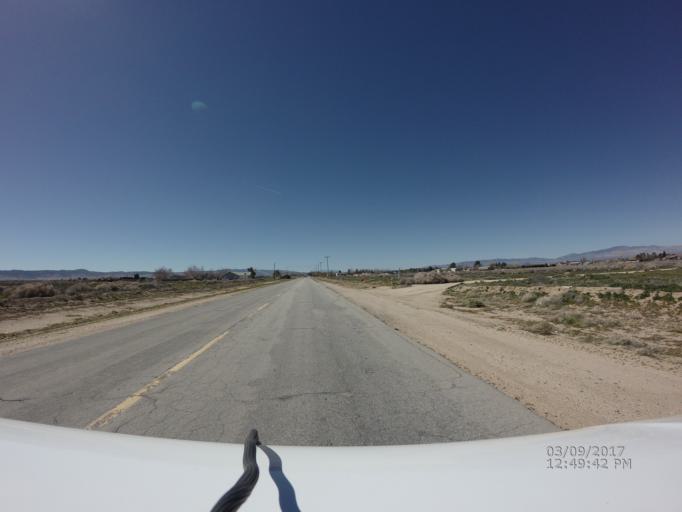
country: US
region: California
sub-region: Los Angeles County
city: Quartz Hill
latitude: 34.7475
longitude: -118.2677
